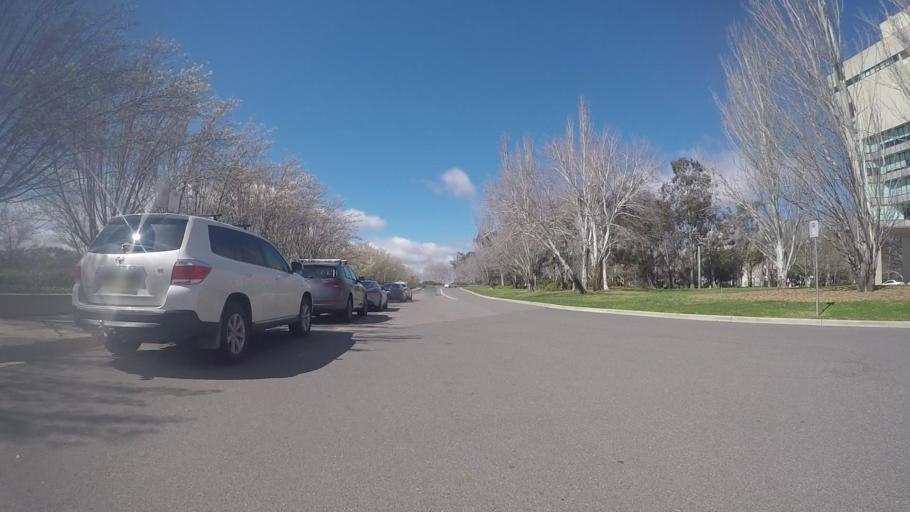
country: AU
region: Australian Capital Territory
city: Canberra
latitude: -35.2981
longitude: 149.1361
